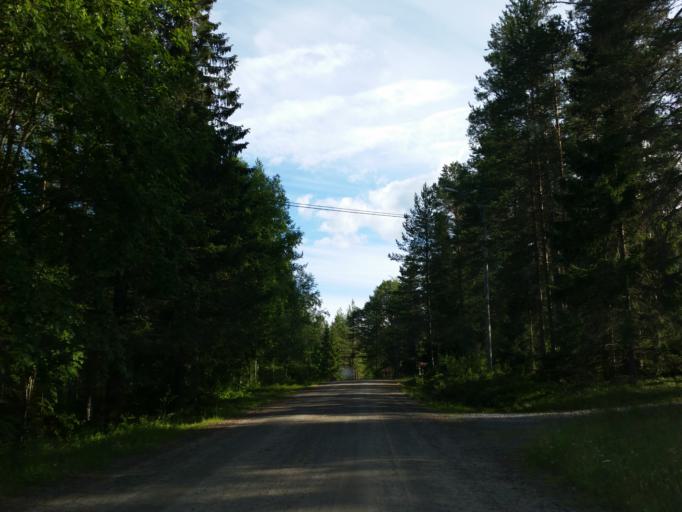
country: SE
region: Vaesterbotten
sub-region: Robertsfors Kommun
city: Robertsfors
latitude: 64.0408
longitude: 20.8500
